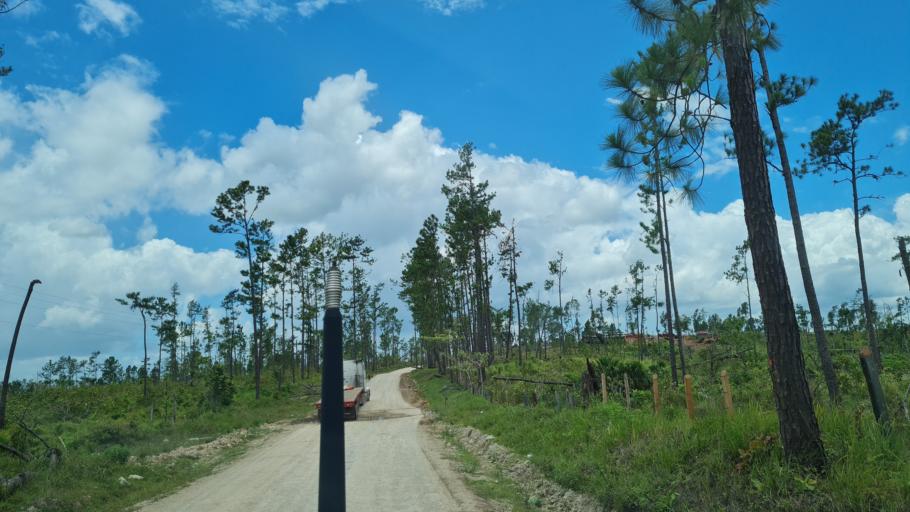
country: NI
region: Atlantico Sur
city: La Cruz de Rio Grande
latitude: 13.5693
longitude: -84.3180
